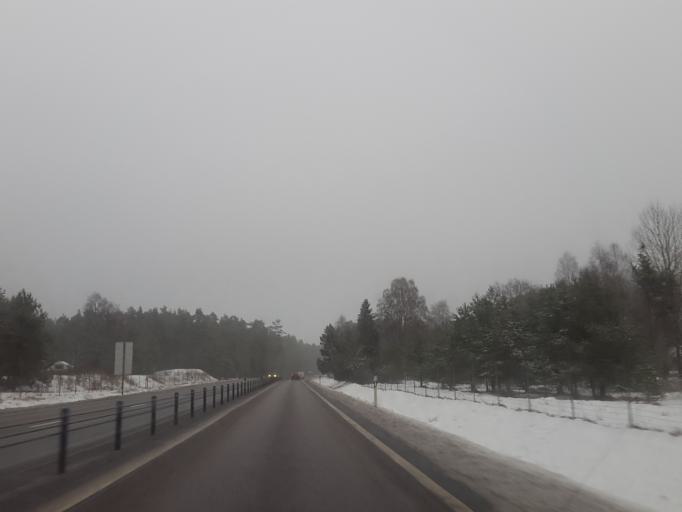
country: SE
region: Joenkoeping
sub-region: Jonkopings Kommun
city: Taberg
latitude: 57.7715
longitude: 14.0438
